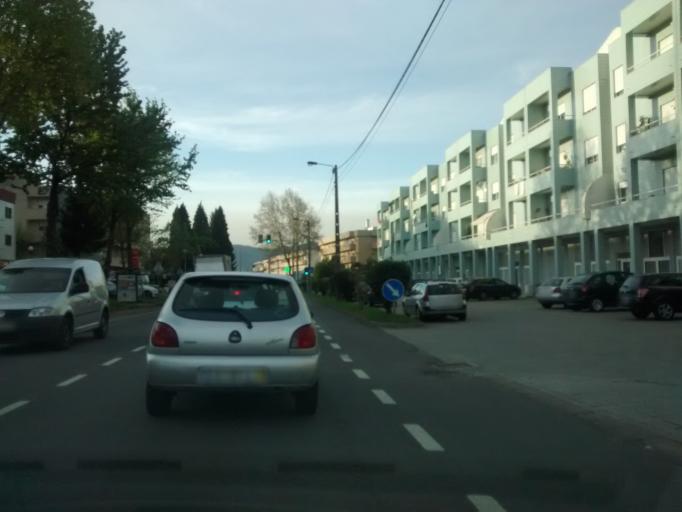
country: PT
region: Braga
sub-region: Guimaraes
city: Ponte
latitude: 41.4773
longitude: -8.3376
